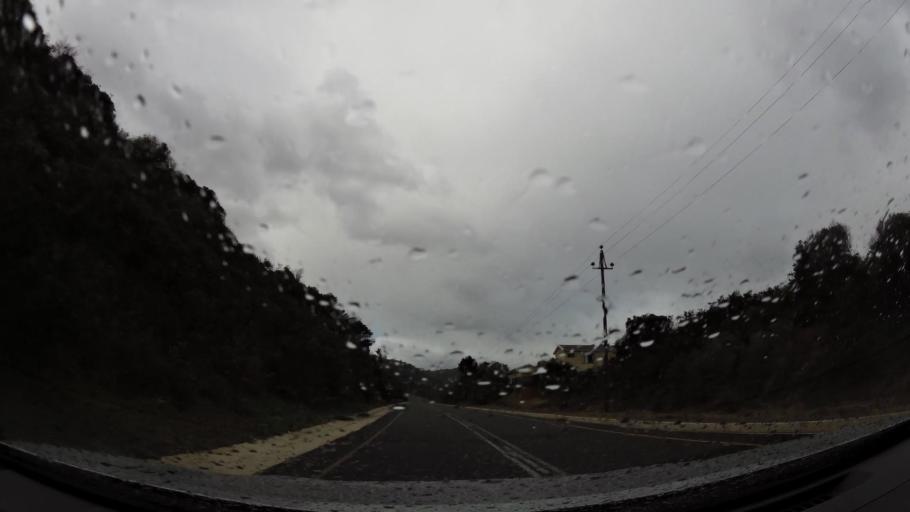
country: ZA
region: Western Cape
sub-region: Eden District Municipality
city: George
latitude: -34.0483
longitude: 22.3062
